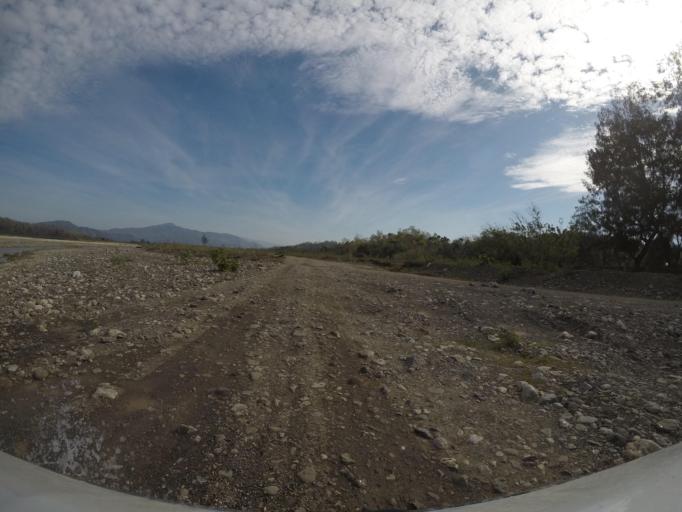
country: TL
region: Bobonaro
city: Maliana
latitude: -8.9028
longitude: 125.2091
